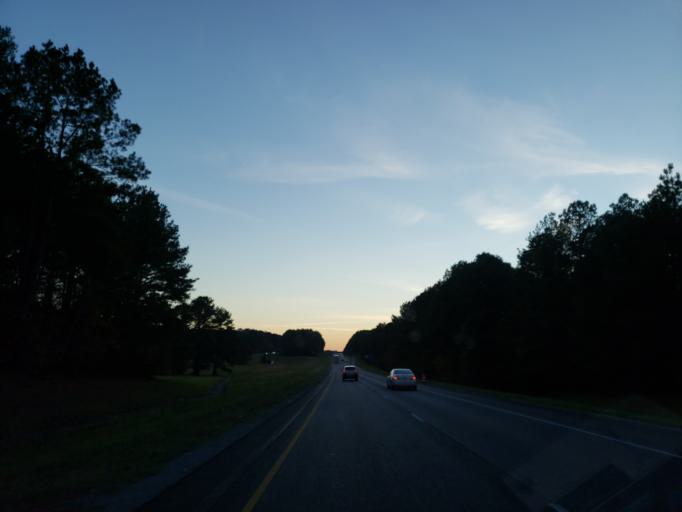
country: US
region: Alabama
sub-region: Sumter County
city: York
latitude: 32.5375
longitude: -88.2846
